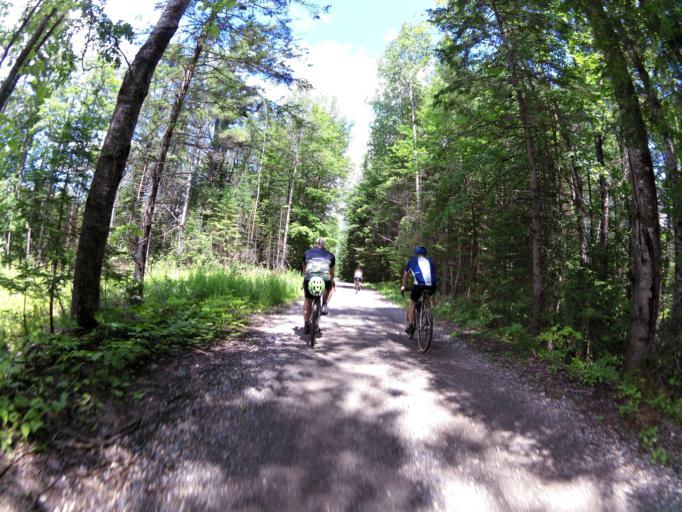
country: CA
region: Ontario
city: Renfrew
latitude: 45.1025
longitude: -76.7055
